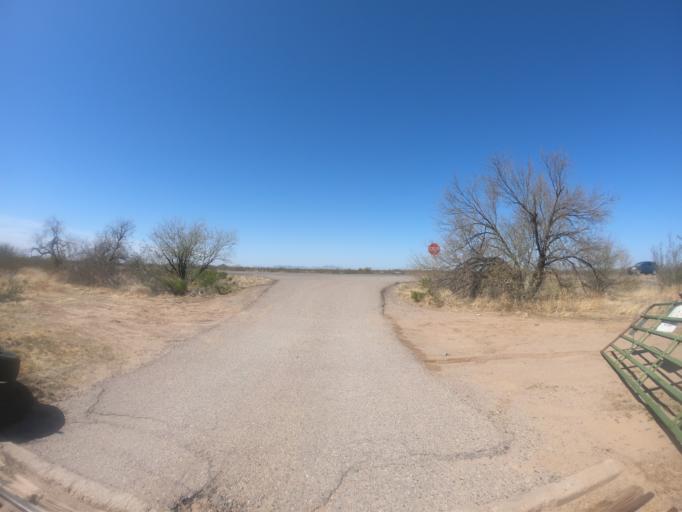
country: US
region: Arizona
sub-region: Pinal County
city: Gold Camp
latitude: 33.2390
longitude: -111.3425
